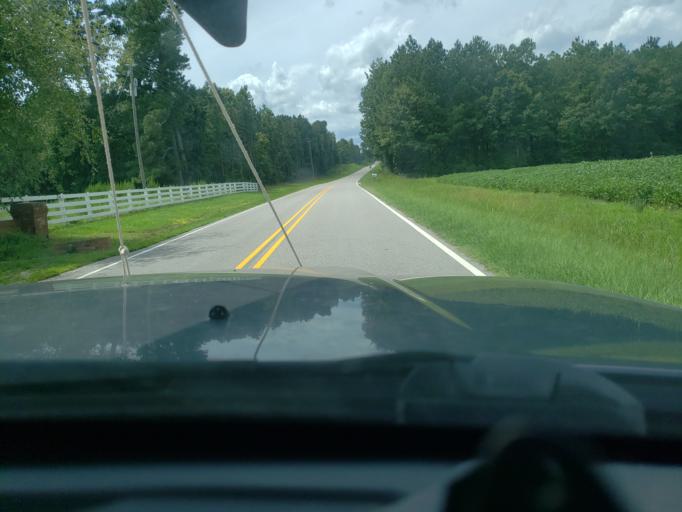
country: US
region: North Carolina
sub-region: Wake County
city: Rolesville
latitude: 35.8830
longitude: -78.4107
